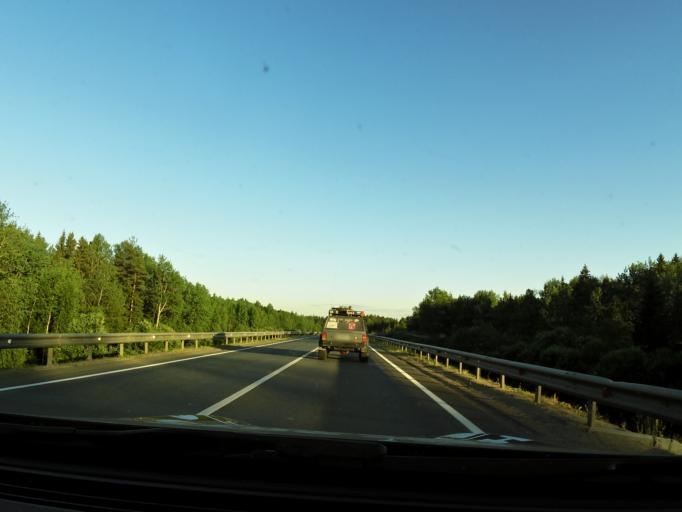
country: RU
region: Vologda
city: Gryazovets
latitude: 58.8548
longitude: 40.2015
